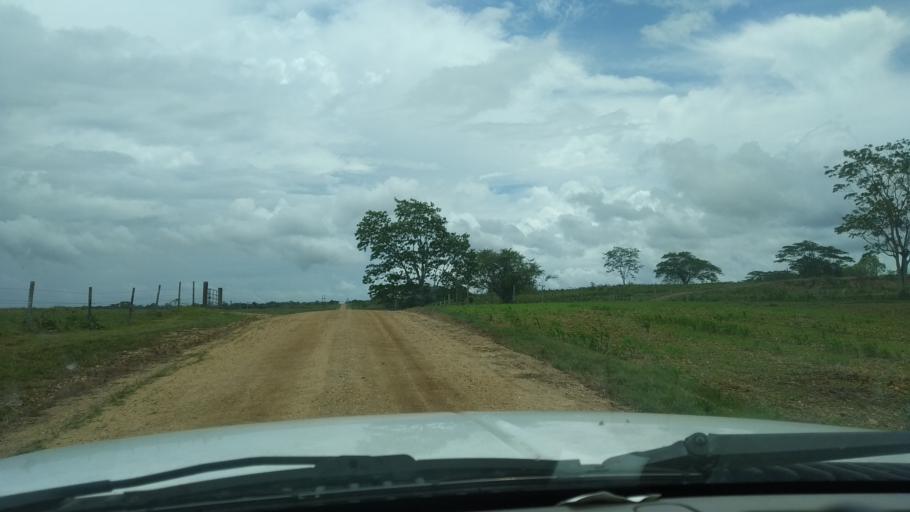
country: BZ
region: Cayo
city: San Ignacio
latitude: 17.2273
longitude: -88.9724
